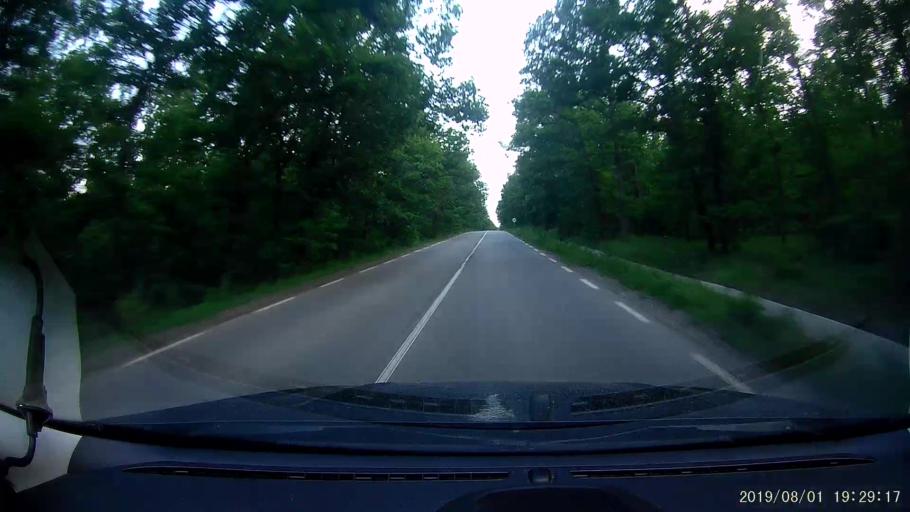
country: BG
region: Burgas
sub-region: Obshtina Sungurlare
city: Sungurlare
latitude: 42.8284
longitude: 26.9089
